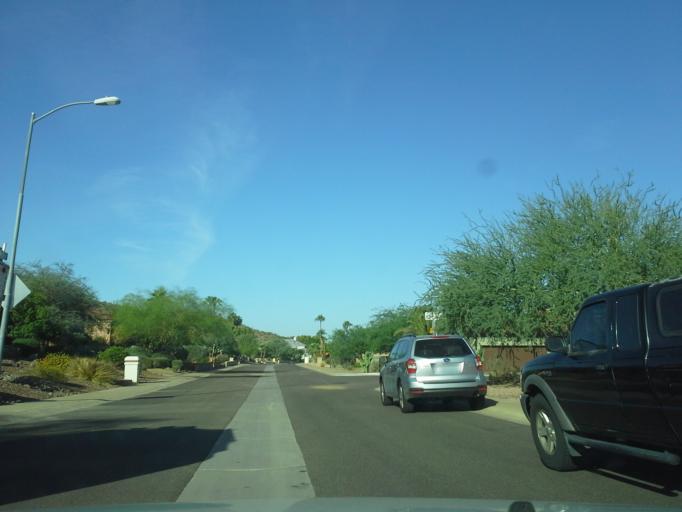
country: US
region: Arizona
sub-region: Maricopa County
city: Glendale
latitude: 33.6026
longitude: -112.0880
